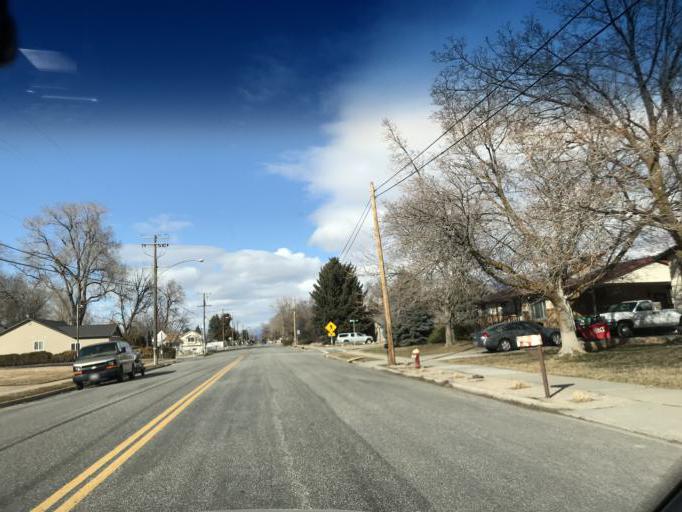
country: US
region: Utah
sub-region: Davis County
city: Woods Cross
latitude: 40.8693
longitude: -111.9021
